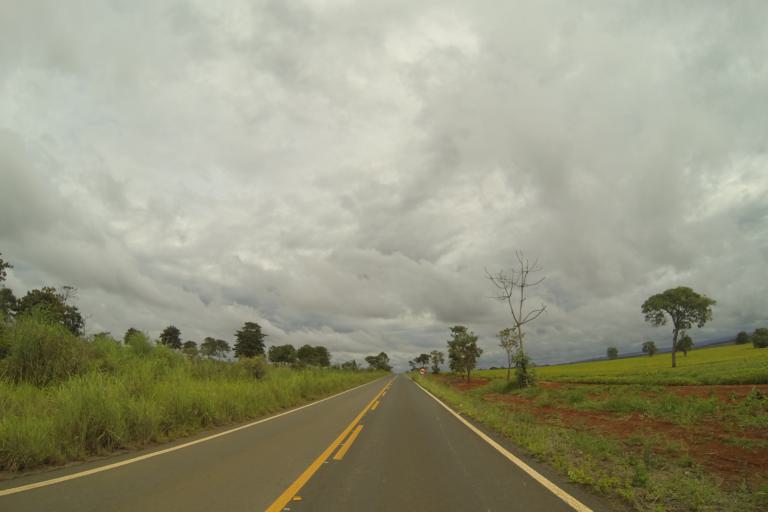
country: BR
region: Minas Gerais
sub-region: Bambui
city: Bambui
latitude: -20.0983
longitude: -46.1227
